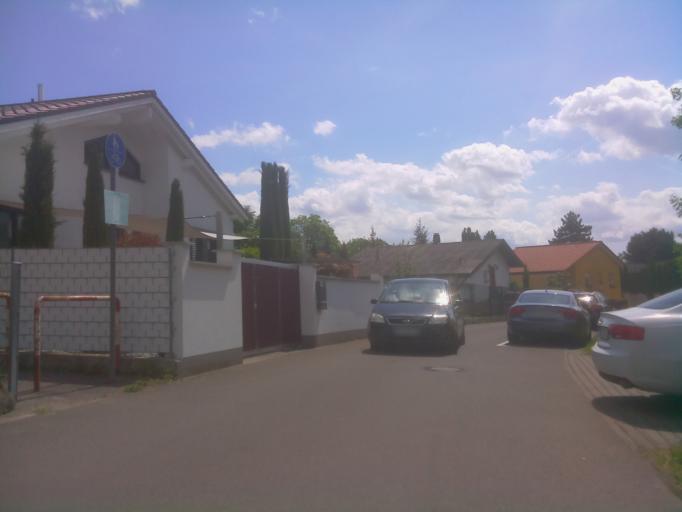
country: DE
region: Rheinland-Pfalz
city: Otterstadt
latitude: 49.3553
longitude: 8.4511
